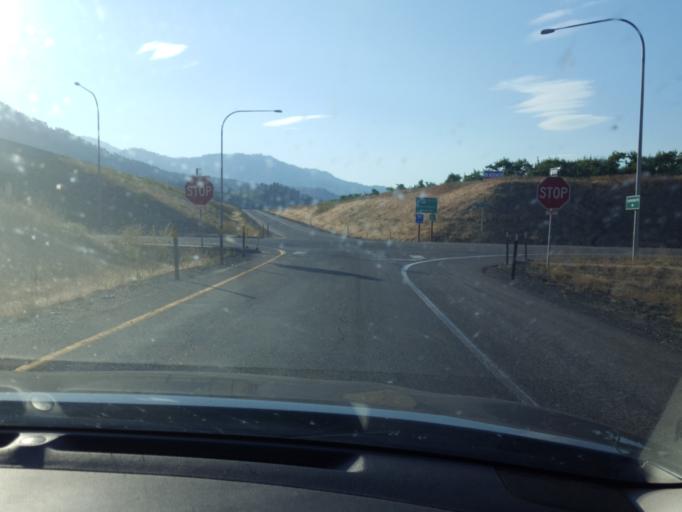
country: US
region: Washington
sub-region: Chelan County
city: Leavenworth
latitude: 47.5588
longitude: -120.5918
